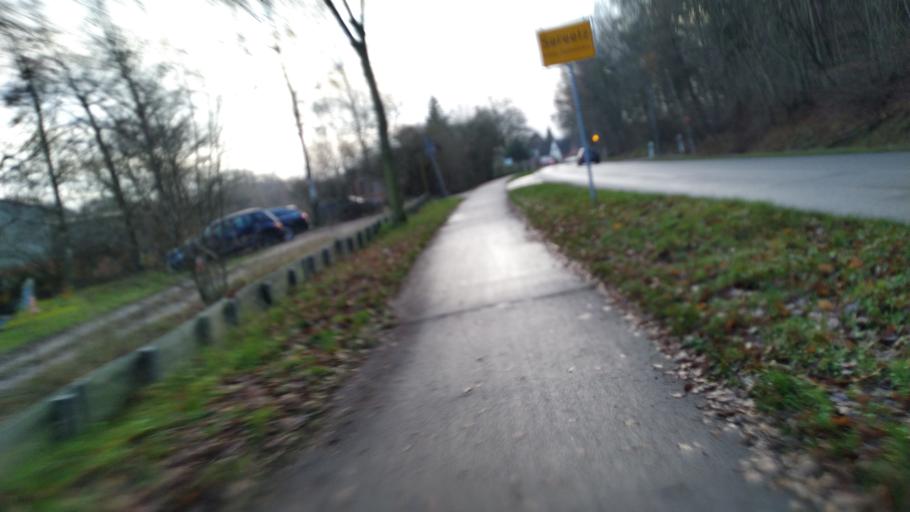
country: DE
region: Schleswig-Holstein
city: Ratekau
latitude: 53.9272
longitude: 10.7385
